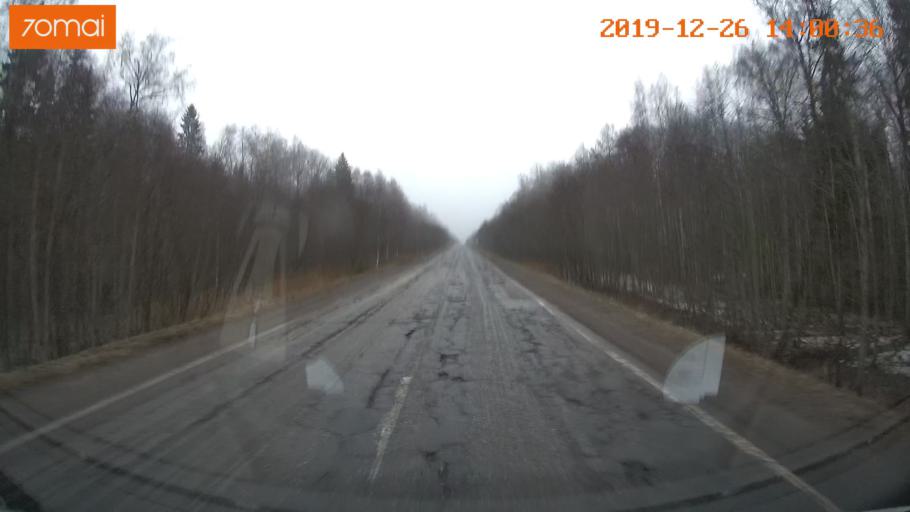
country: RU
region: Jaroslavl
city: Poshekhon'ye
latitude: 58.5570
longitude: 38.7466
